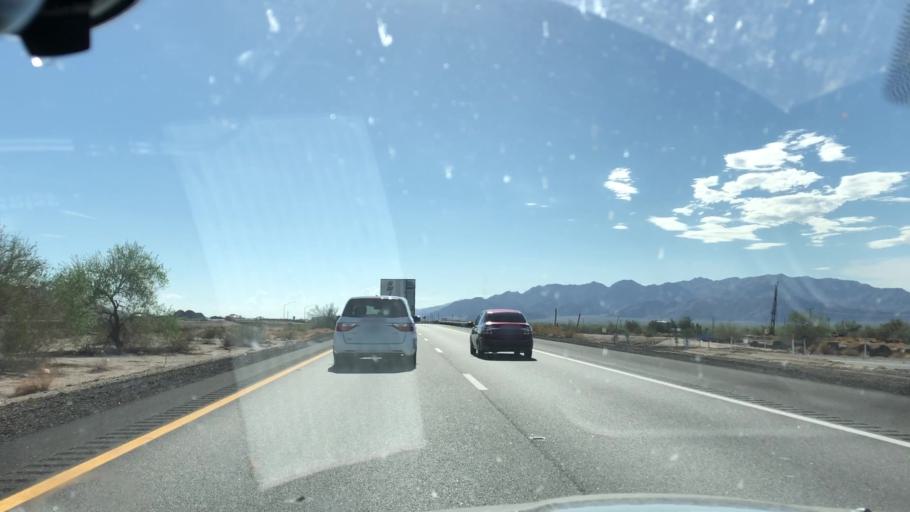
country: US
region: California
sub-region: Imperial County
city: Niland
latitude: 33.7107
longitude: -115.3981
